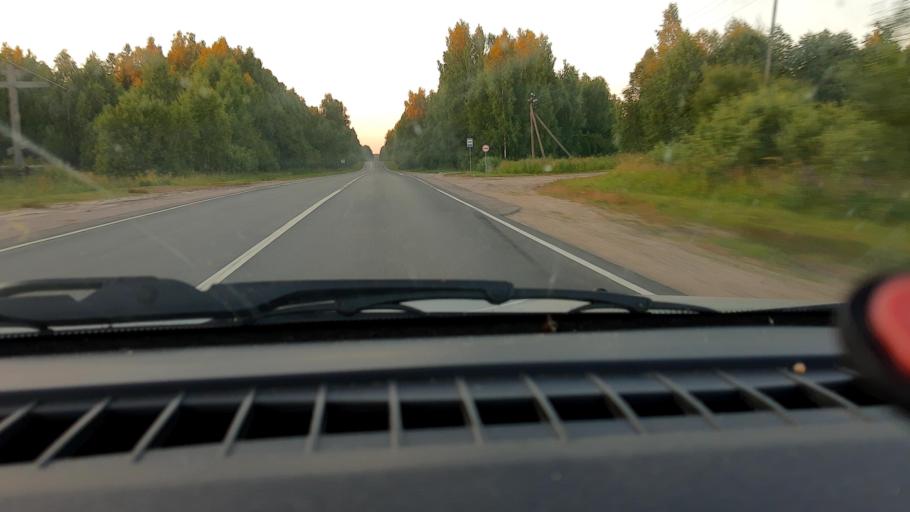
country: RU
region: Nizjnij Novgorod
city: Uren'
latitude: 57.2749
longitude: 45.6313
